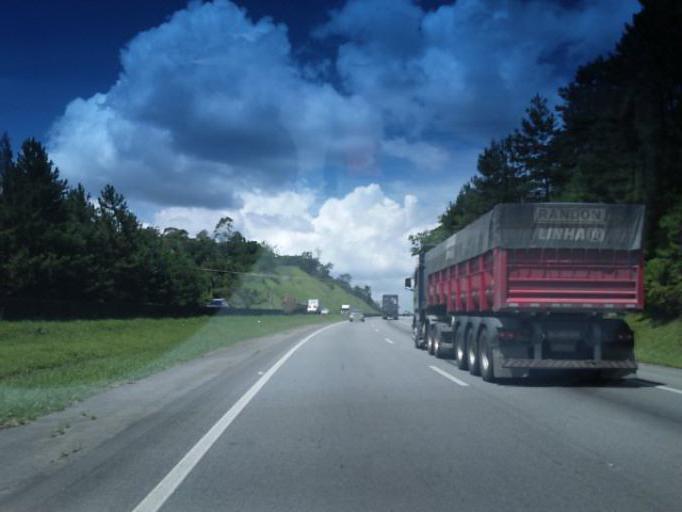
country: BR
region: Sao Paulo
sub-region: Juquitiba
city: Juquitiba
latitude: -23.9631
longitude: -47.1232
